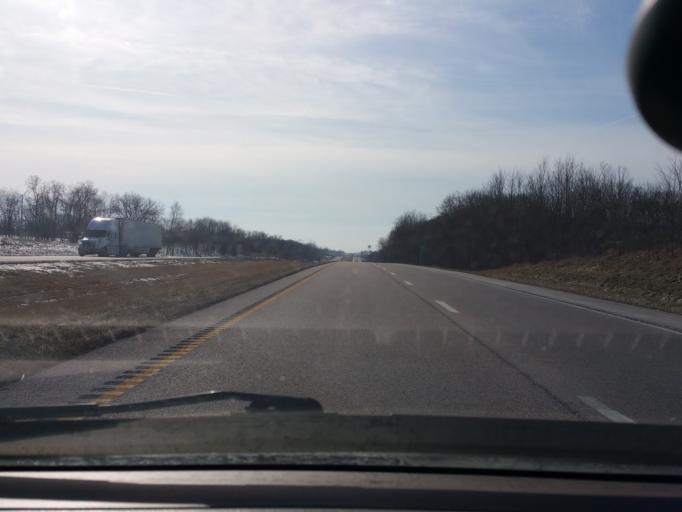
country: US
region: Missouri
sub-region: Clinton County
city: Lathrop
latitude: 39.4755
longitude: -94.3112
